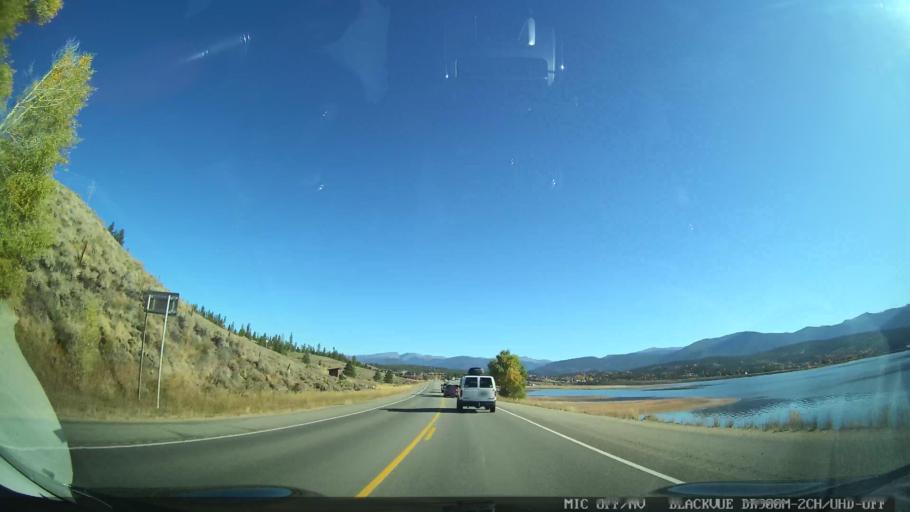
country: US
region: Colorado
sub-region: Grand County
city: Granby
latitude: 40.1847
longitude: -105.8854
